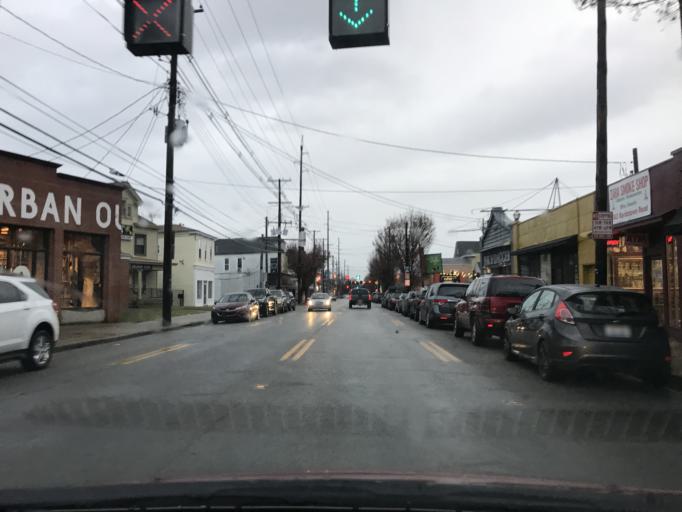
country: US
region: Kentucky
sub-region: Jefferson County
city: Audubon Park
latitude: 38.2374
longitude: -85.7191
